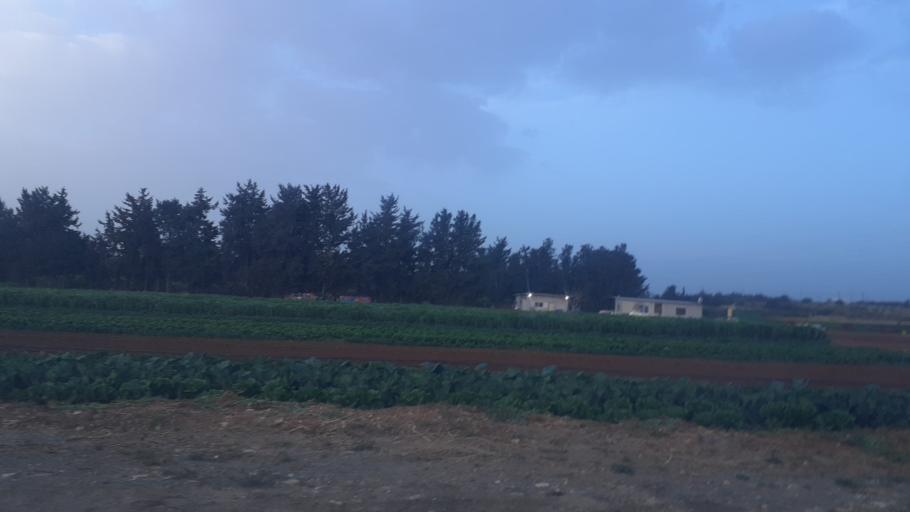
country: CY
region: Limassol
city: Ypsonas
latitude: 34.6716
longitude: 32.9829
